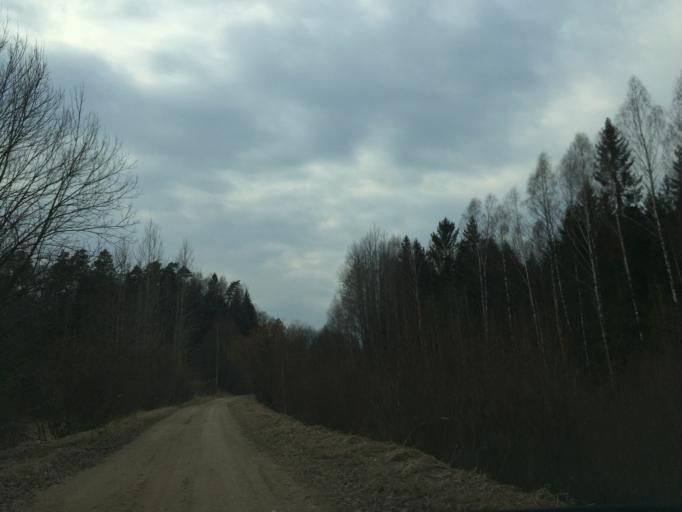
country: LV
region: Amatas Novads
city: Drabesi
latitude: 57.1973
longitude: 25.3679
